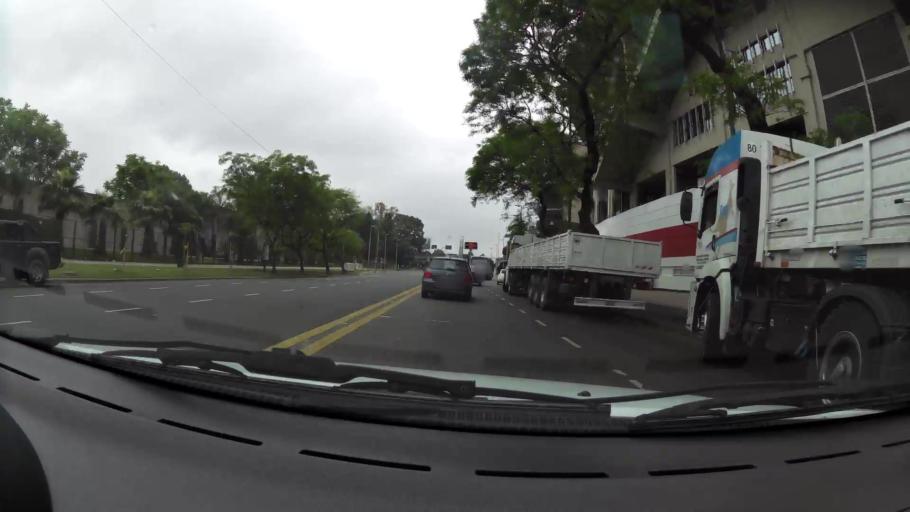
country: AR
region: Buenos Aires F.D.
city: Colegiales
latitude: -34.5448
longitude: -58.4509
